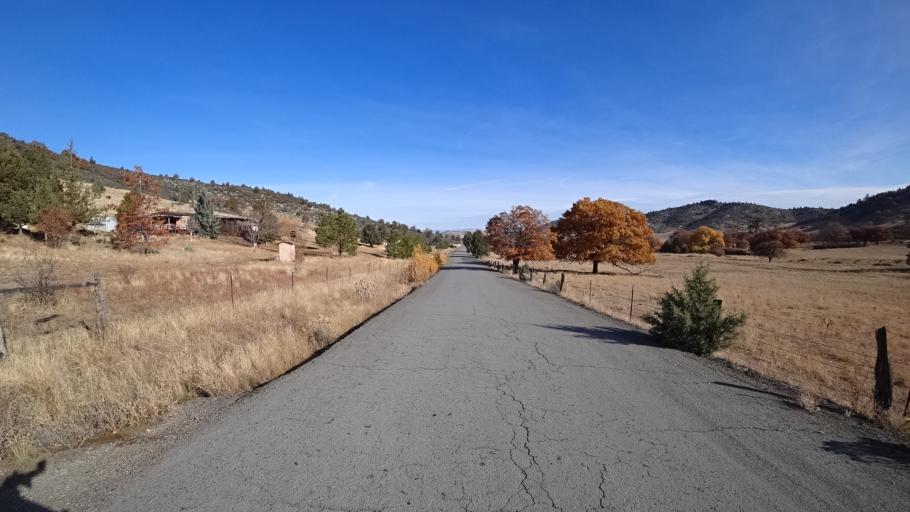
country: US
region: California
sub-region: Siskiyou County
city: Montague
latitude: 41.6257
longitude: -122.5734
